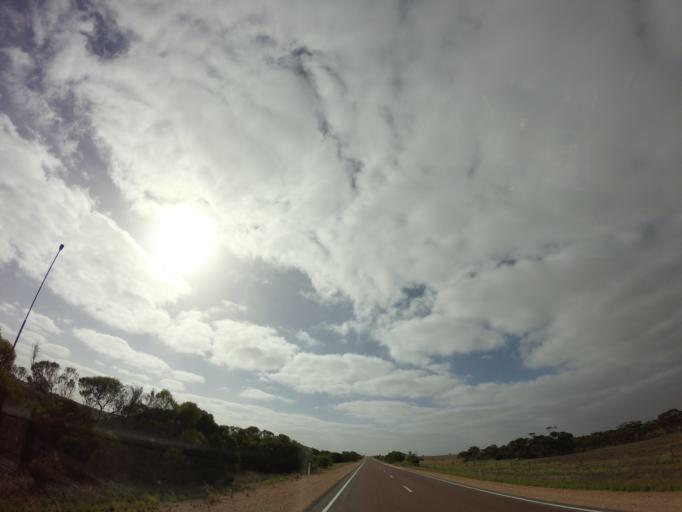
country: AU
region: South Australia
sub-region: Streaky Bay
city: Streaky Bay
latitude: -32.2669
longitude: 134.2032
